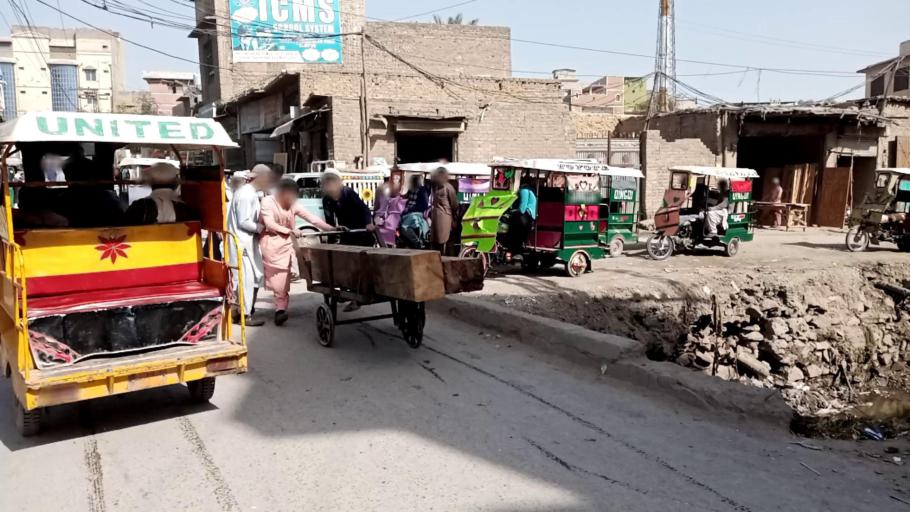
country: PK
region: Khyber Pakhtunkhwa
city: Peshawar
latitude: 34.0038
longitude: 71.5782
